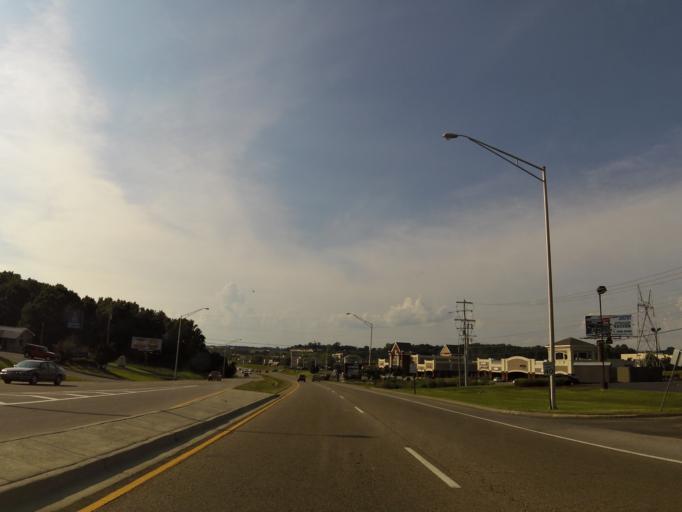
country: US
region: Tennessee
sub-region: Loudon County
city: Lenoir City
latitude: 35.8164
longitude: -84.2646
